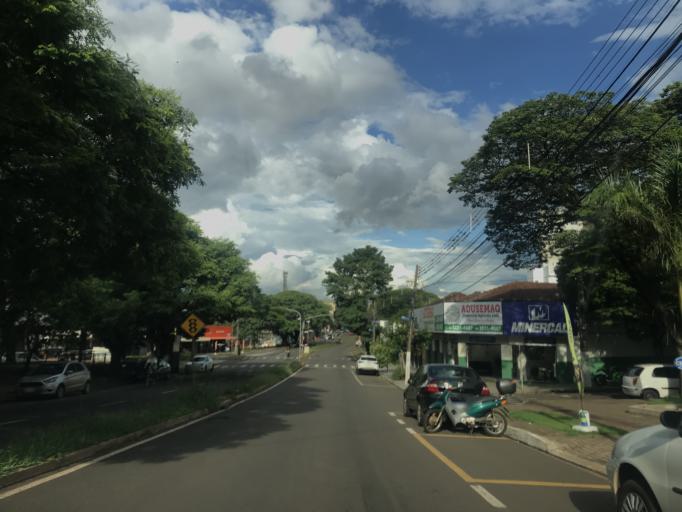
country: BR
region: Parana
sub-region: Maringa
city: Maringa
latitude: -23.4249
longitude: -51.9605
